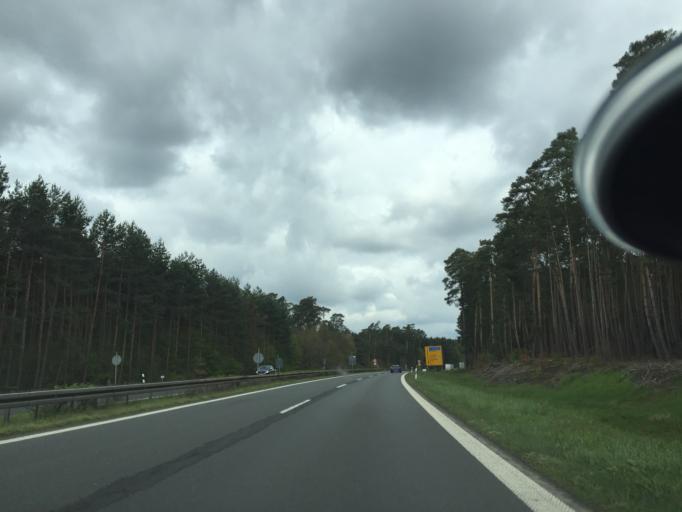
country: DE
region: Bavaria
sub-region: Regierungsbezirk Unterfranken
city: Stockstadt am Main
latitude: 49.9482
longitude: 9.0568
